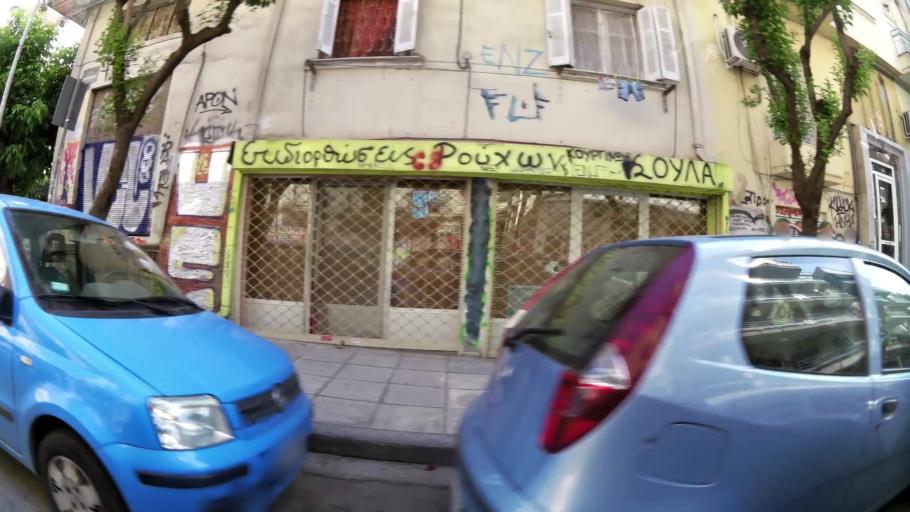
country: GR
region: Central Macedonia
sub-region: Nomos Thessalonikis
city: Agios Pavlos
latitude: 40.6345
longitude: 22.9522
